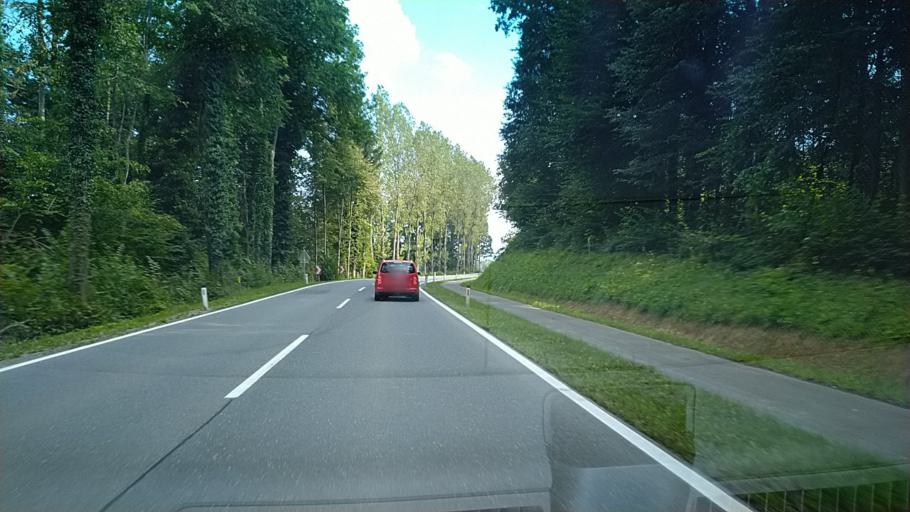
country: AT
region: Styria
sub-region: Politischer Bezirk Deutschlandsberg
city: Hollenegg
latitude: 46.7879
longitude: 15.2285
